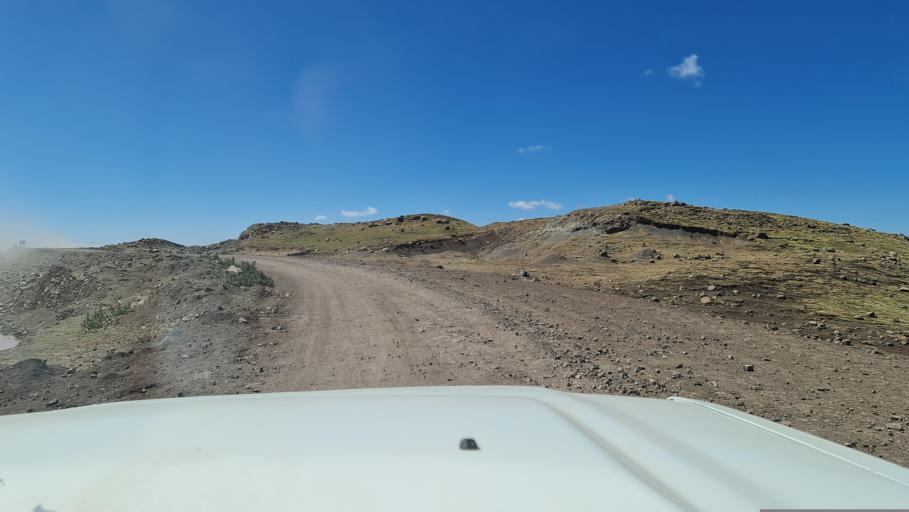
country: ET
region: Amhara
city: Debark'
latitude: 13.2409
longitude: 38.1180
